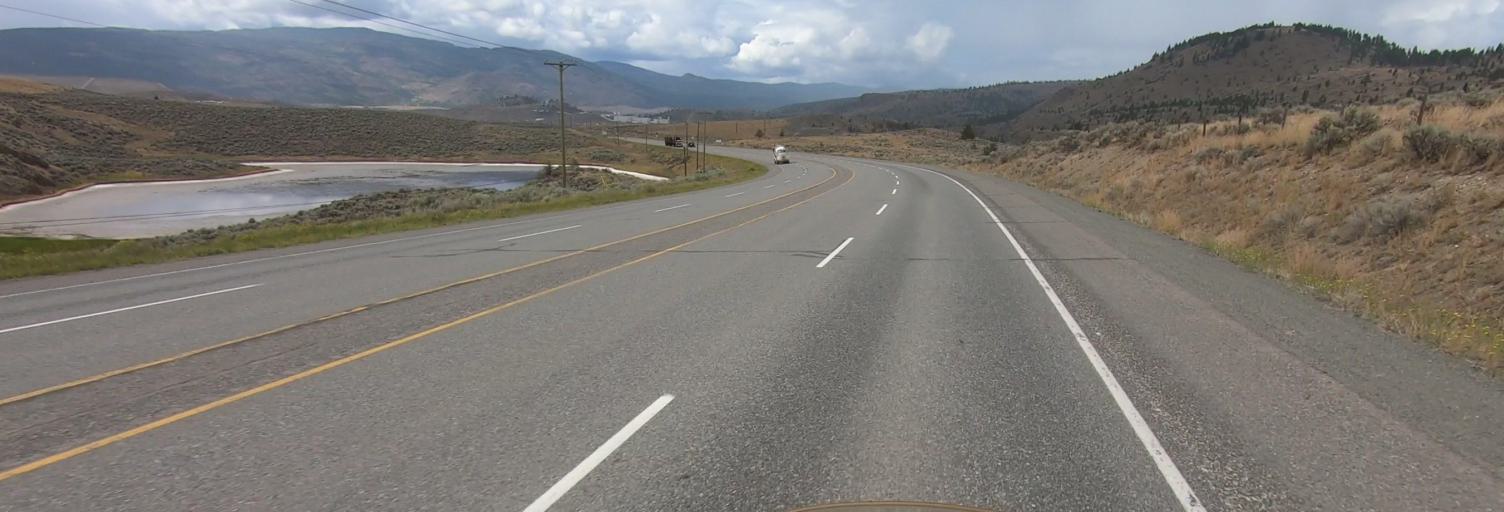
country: CA
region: British Columbia
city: Kamloops
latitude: 50.6690
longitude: -120.4803
